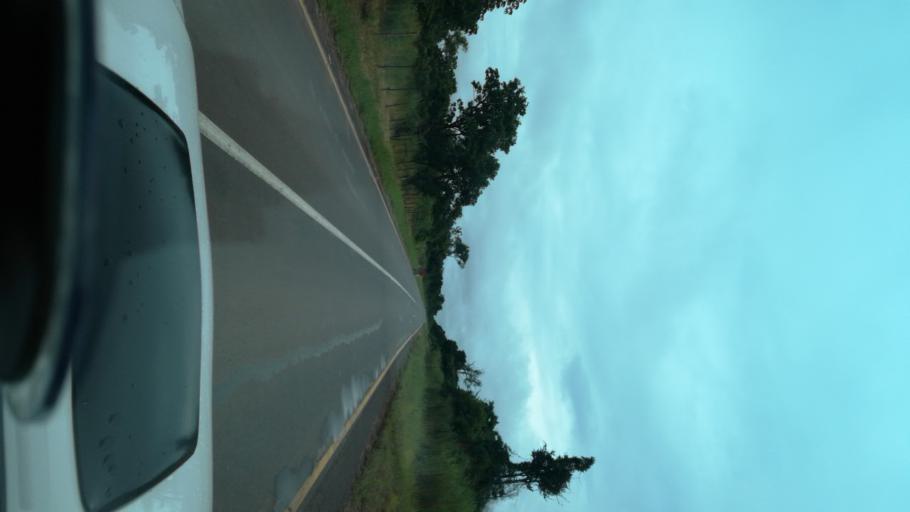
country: CD
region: Katanga
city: Lubumbashi
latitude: -11.2340
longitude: 27.8921
